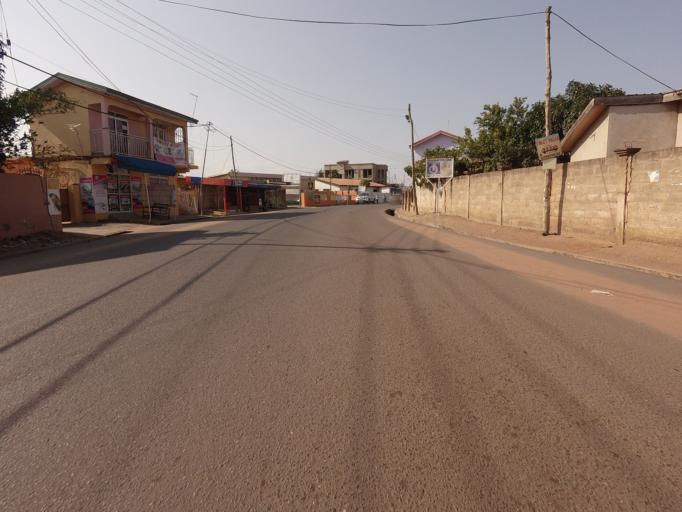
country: GH
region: Greater Accra
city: Nungua
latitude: 5.6245
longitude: -0.0910
